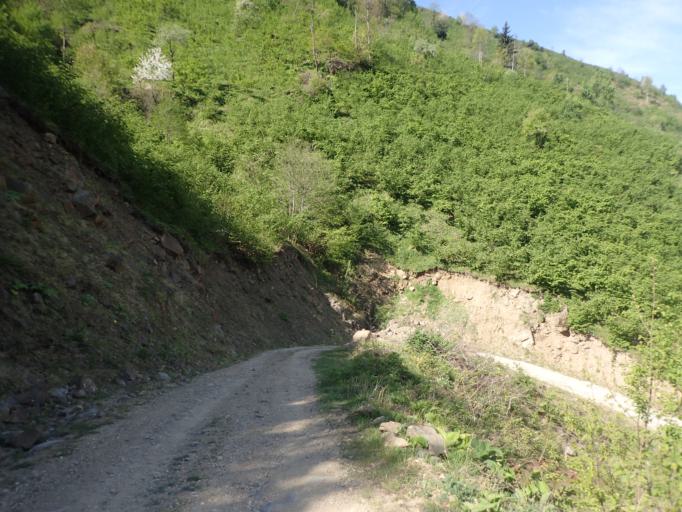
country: TR
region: Ordu
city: Topcam
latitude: 40.7091
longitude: 37.8745
